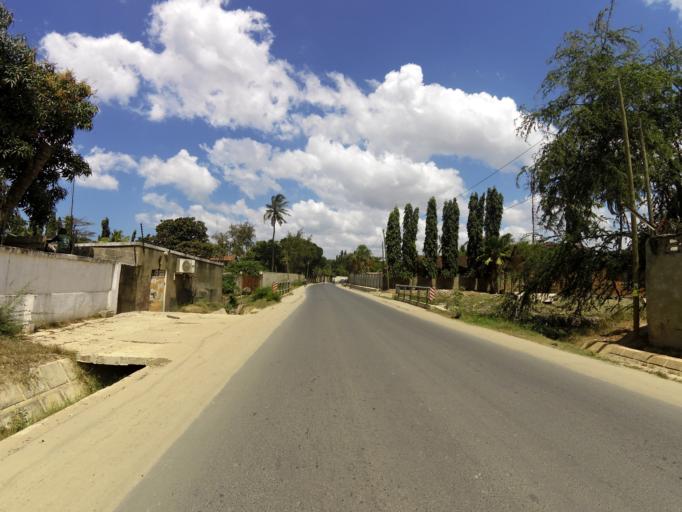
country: TZ
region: Dar es Salaam
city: Magomeni
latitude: -6.7691
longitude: 39.2511
